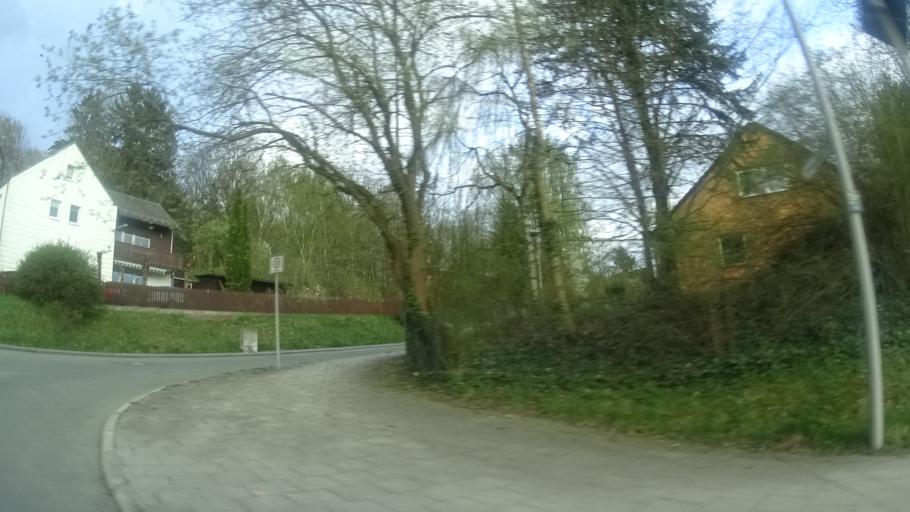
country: DE
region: Bavaria
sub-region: Upper Franconia
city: Hof
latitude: 50.2998
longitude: 11.8898
